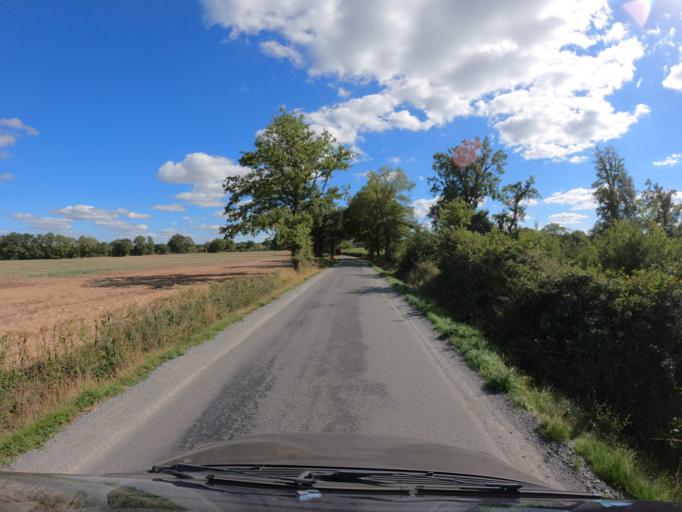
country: FR
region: Auvergne
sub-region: Departement de l'Allier
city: Doyet
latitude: 46.3931
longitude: 2.7554
